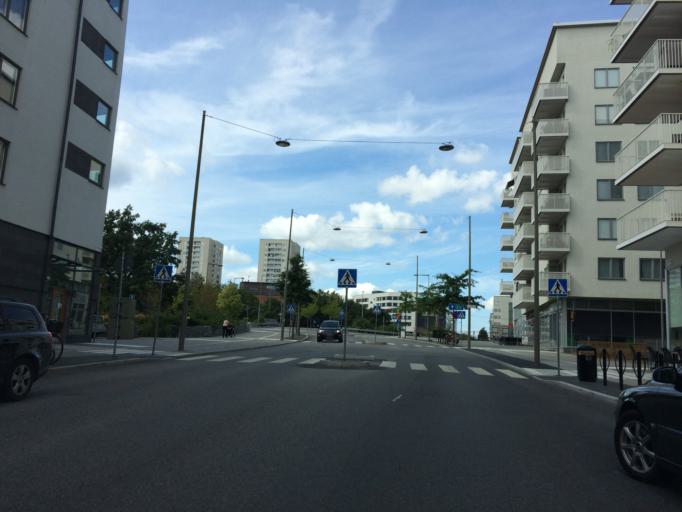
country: SE
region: Stockholm
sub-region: Stockholms Kommun
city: Arsta
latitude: 59.3078
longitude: 18.0277
